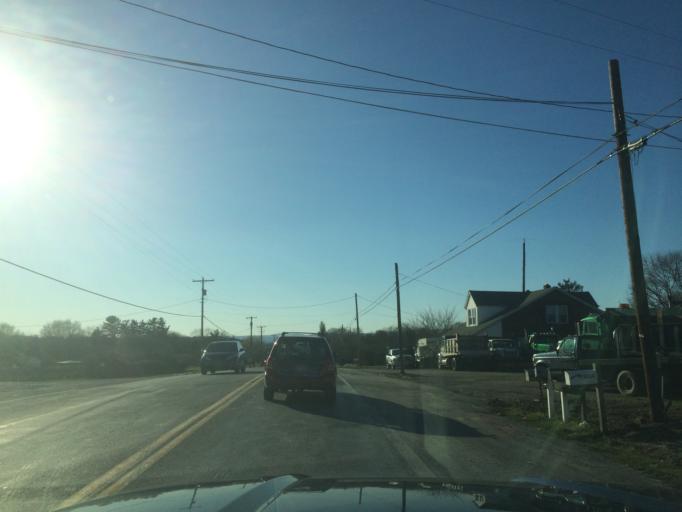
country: US
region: Maryland
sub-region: Frederick County
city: Spring Ridge
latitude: 39.3904
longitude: -77.3127
